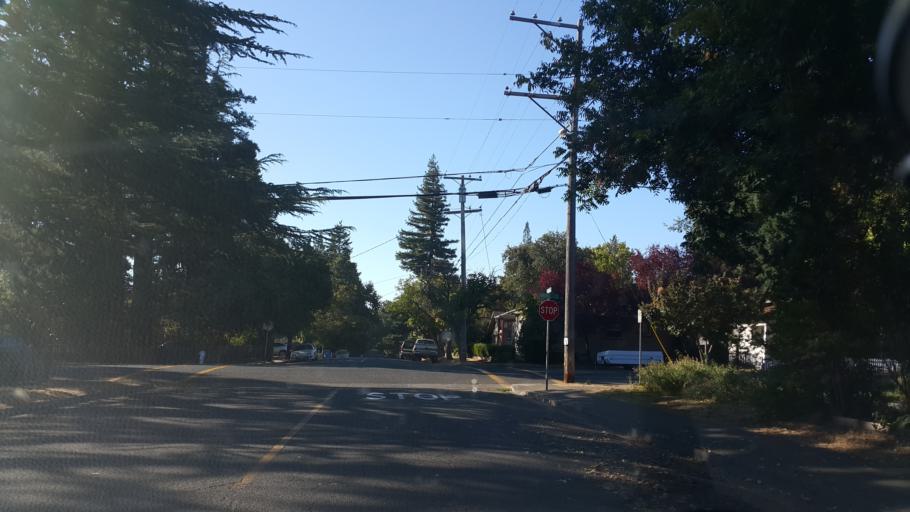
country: US
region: California
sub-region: Mendocino County
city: Ukiah
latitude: 39.1538
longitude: -123.2157
